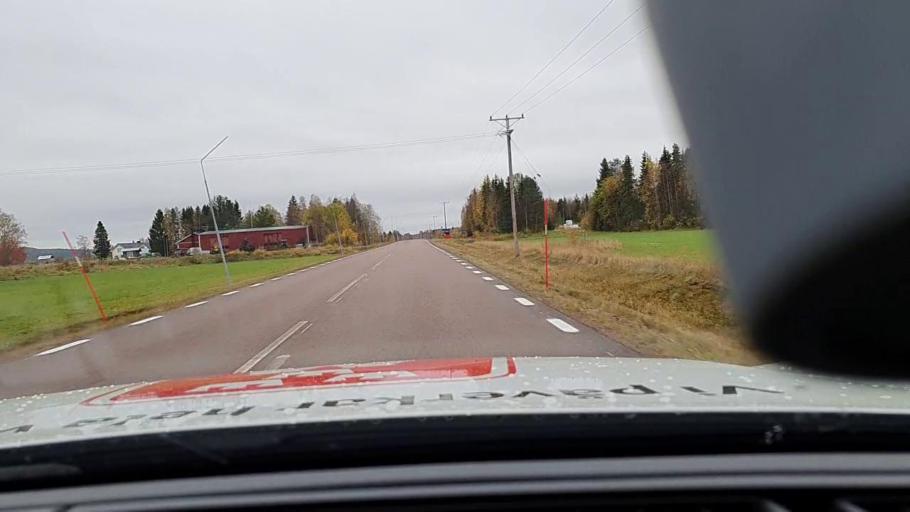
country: FI
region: Lapland
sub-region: Torniolaakso
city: Ylitornio
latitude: 66.1426
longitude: 23.8980
